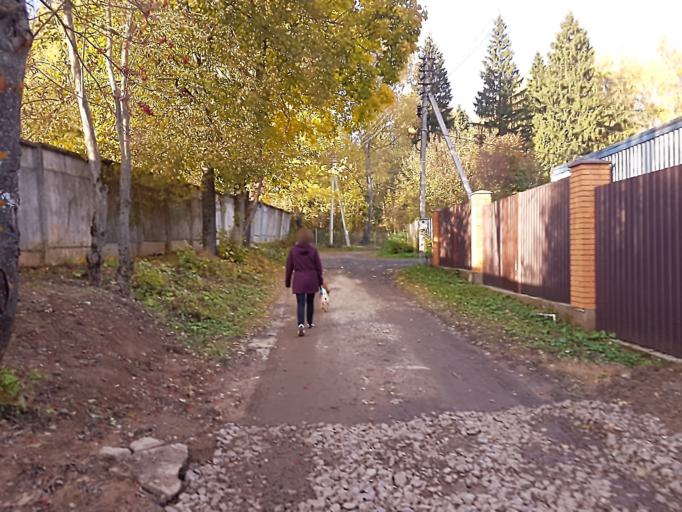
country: RU
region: Moskovskaya
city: Istra
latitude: 55.9184
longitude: 36.8829
